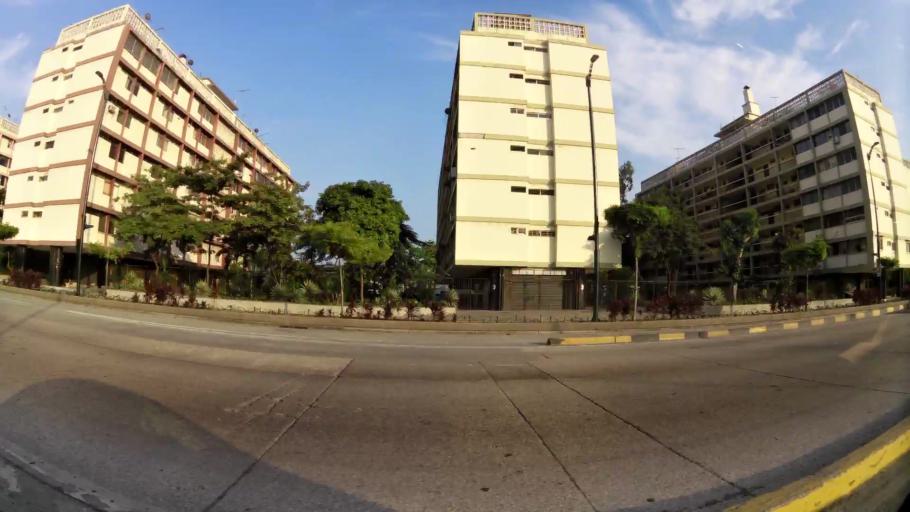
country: EC
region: Guayas
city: Guayaquil
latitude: -2.2096
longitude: -79.8954
